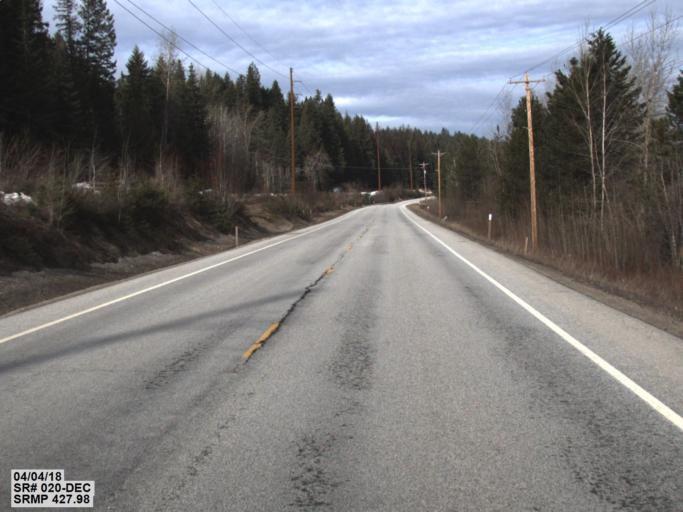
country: US
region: Washington
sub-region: Pend Oreille County
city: Newport
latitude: 48.2315
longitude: -117.2053
